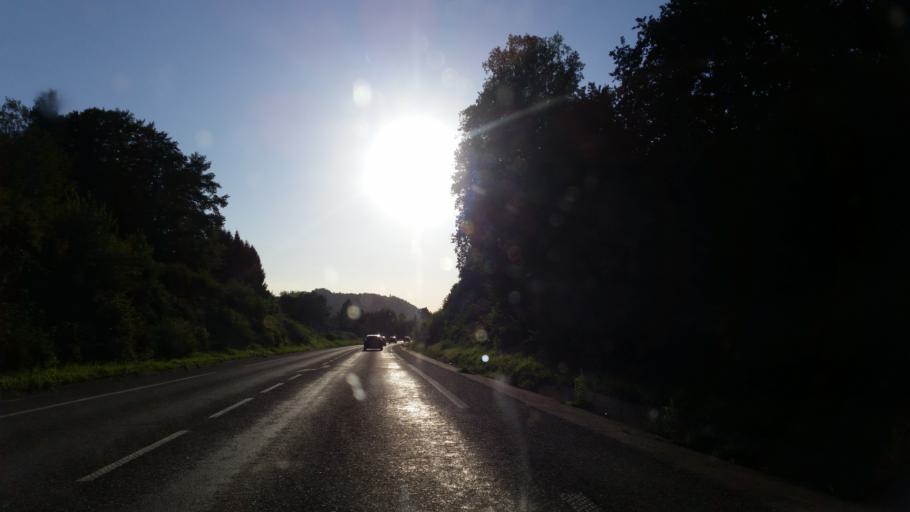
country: FR
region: Lorraine
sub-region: Departement des Vosges
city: Saint-Etienne-les-Remiremont
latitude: 48.0159
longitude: 6.6211
